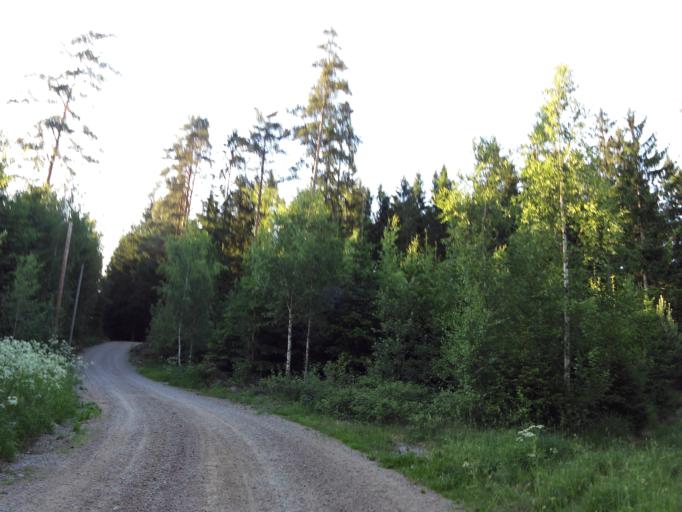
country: SE
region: Blekinge
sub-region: Olofstroms Kommun
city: Olofstroem
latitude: 56.4054
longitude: 14.5660
